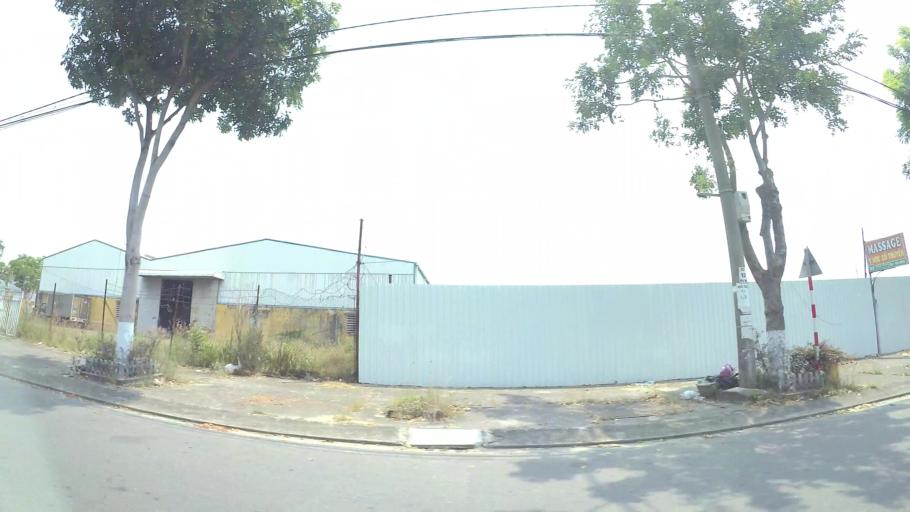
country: VN
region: Da Nang
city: Cam Le
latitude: 16.0036
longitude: 108.2073
